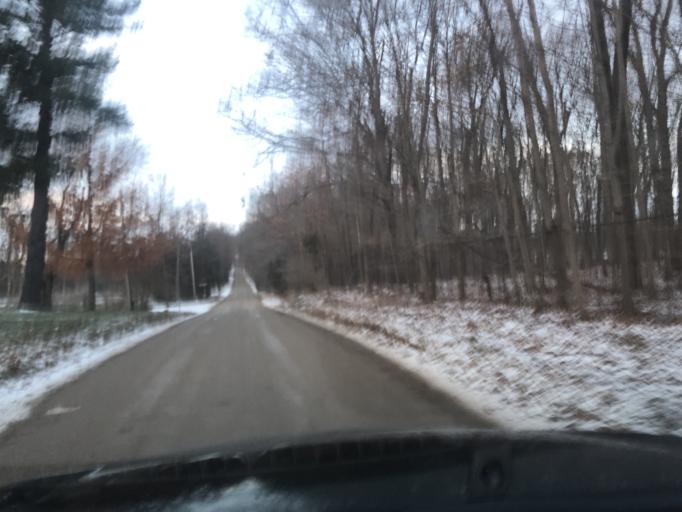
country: US
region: Michigan
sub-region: Oakland County
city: Milford
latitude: 42.5888
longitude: -83.6402
